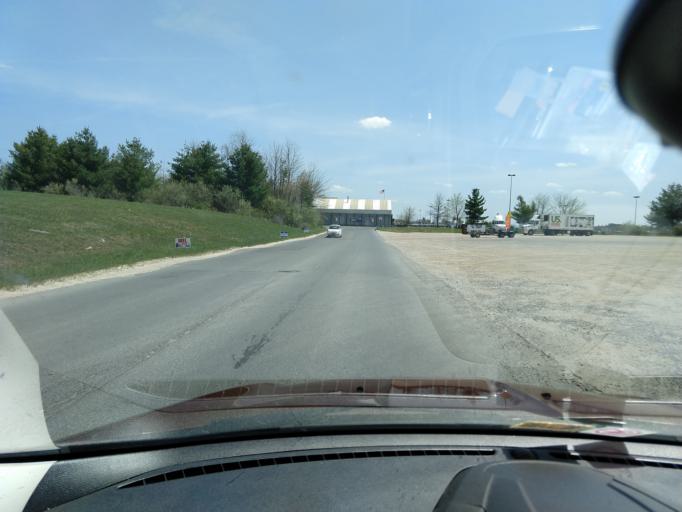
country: US
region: West Virginia
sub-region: Raleigh County
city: Stanaford
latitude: 37.8068
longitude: -81.1789
